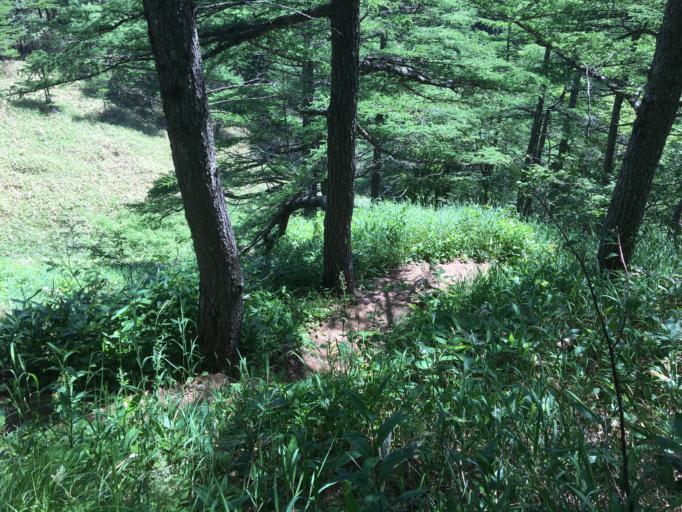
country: JP
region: Nagano
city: Komoro
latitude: 36.4041
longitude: 138.4760
